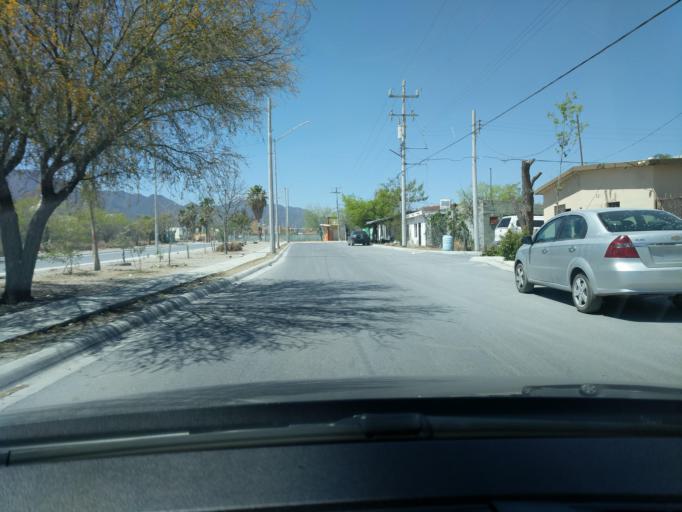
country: MX
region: Nuevo Leon
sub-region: Salinas Victoria
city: Las Torres
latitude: 25.9619
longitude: -100.3029
